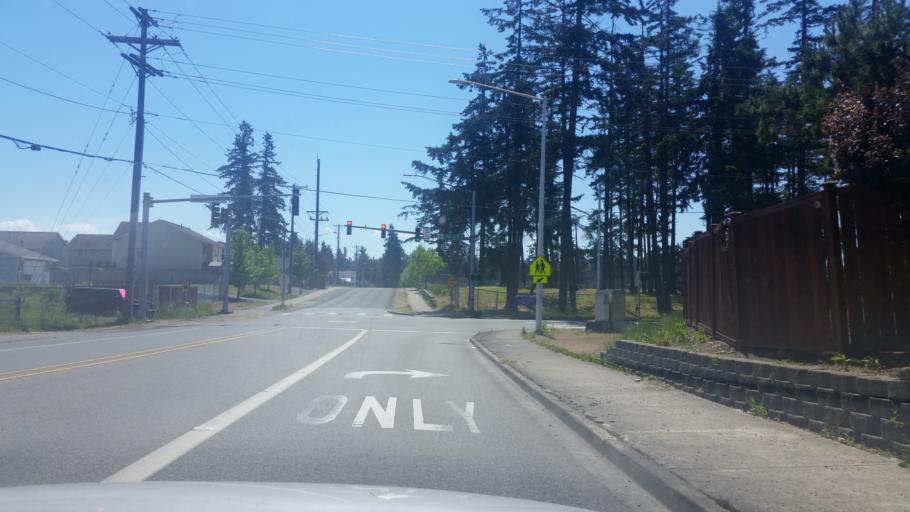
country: US
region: Washington
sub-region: Pierce County
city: Graham
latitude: 47.0719
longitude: -122.3262
